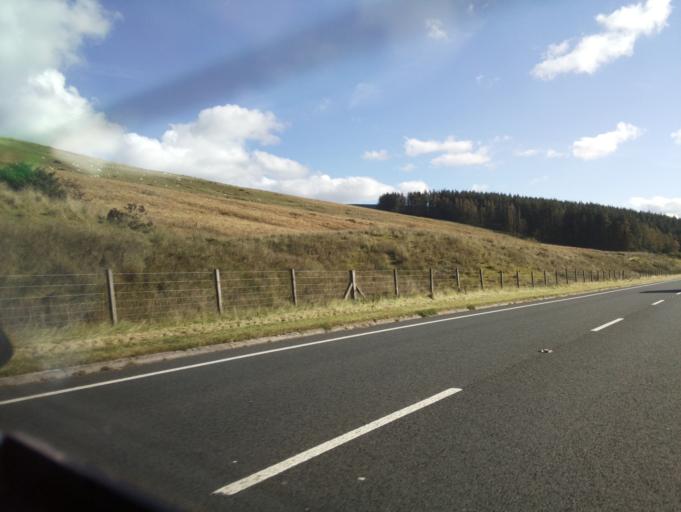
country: GB
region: Wales
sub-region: Rhondda Cynon Taf
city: Hirwaun
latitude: 51.8482
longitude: -3.4661
